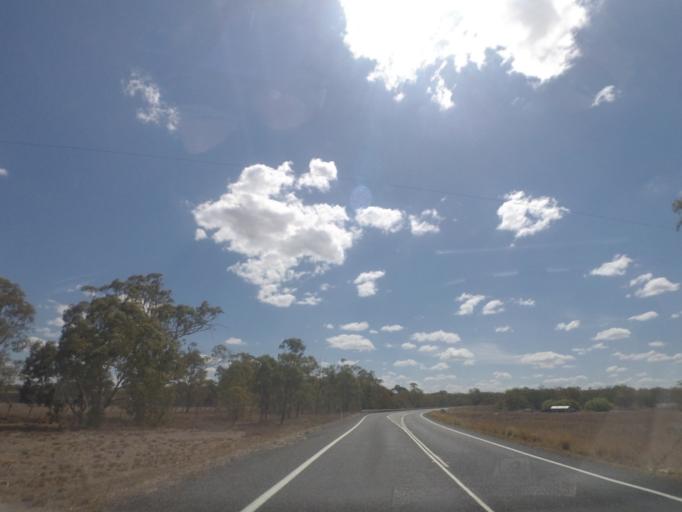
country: AU
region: Queensland
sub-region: Southern Downs
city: Warwick
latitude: -28.1627
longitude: 151.7007
